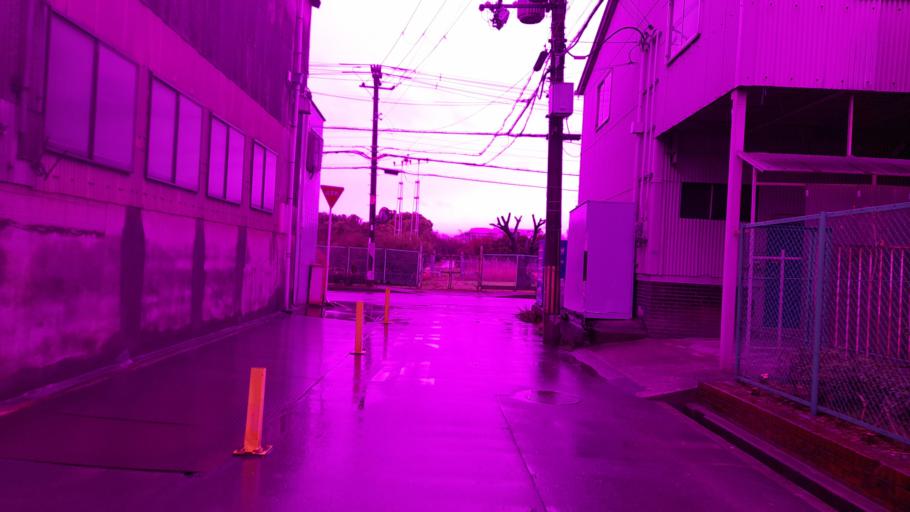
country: JP
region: Osaka
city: Toyonaka
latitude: 34.7695
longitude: 135.4557
